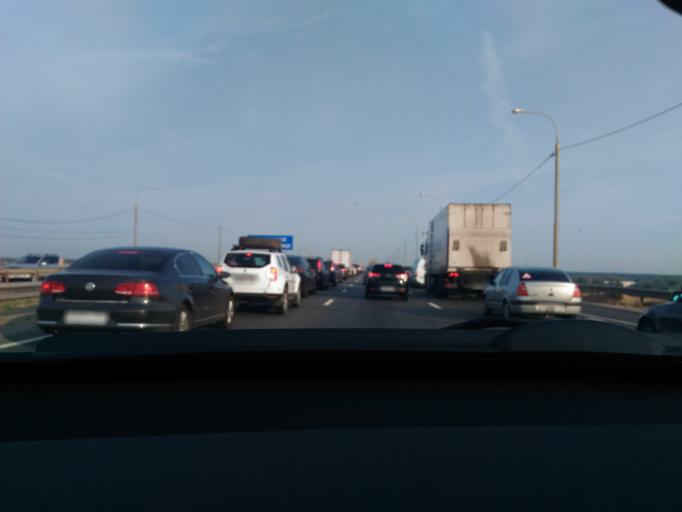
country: RU
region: Moskovskaya
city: Dolgoprudnyy
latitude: 55.9701
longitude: 37.5313
